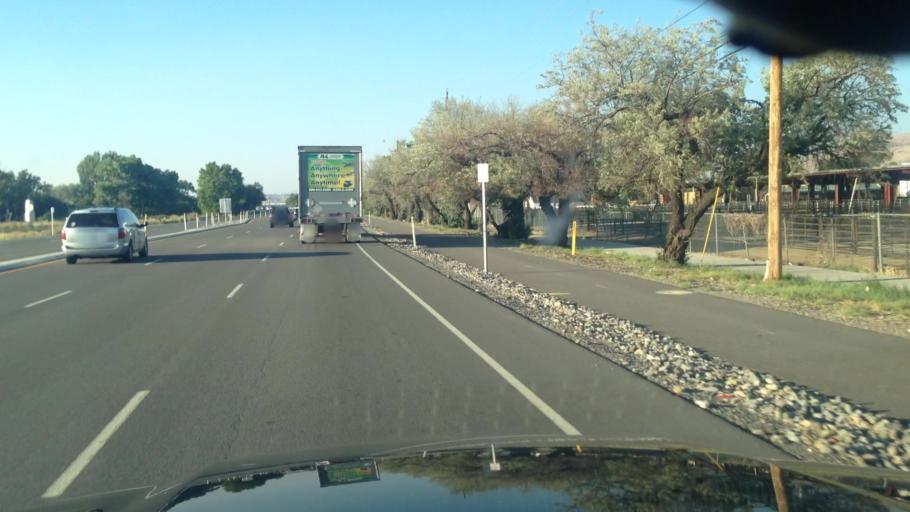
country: US
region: Nevada
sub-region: Washoe County
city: Sparks
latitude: 39.5133
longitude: -119.7432
